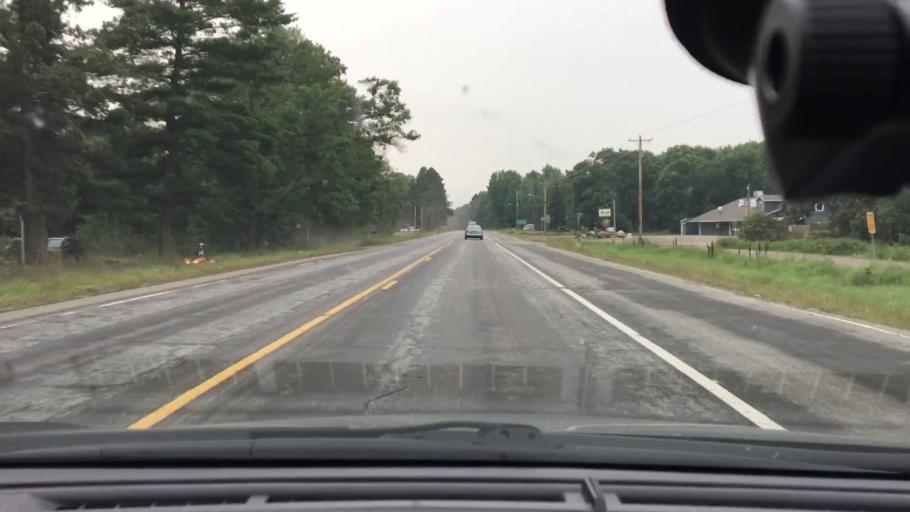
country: US
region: Minnesota
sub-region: Crow Wing County
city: Cross Lake
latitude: 46.7902
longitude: -93.9660
